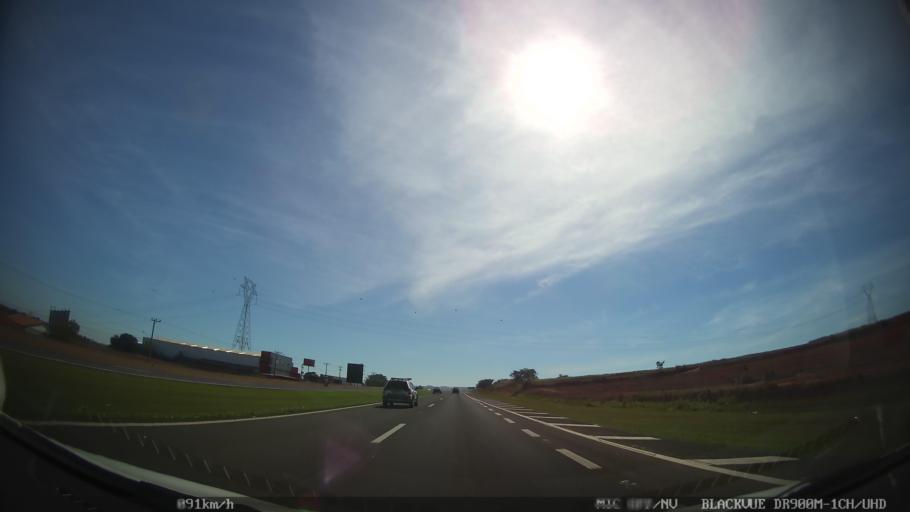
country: BR
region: Sao Paulo
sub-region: Porto Ferreira
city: Porto Ferreira
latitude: -21.8309
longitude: -47.4953
